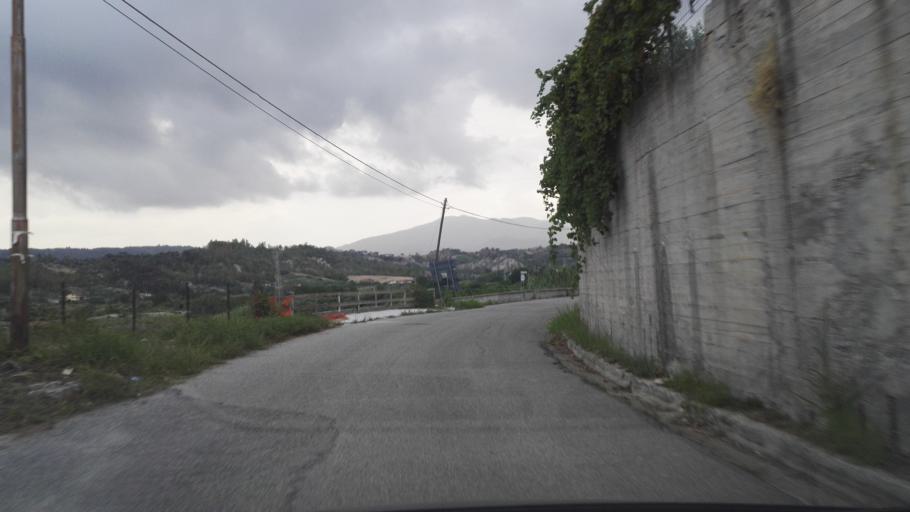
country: IT
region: Calabria
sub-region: Provincia di Reggio Calabria
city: Caulonia Marina
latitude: 38.3634
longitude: 16.4598
